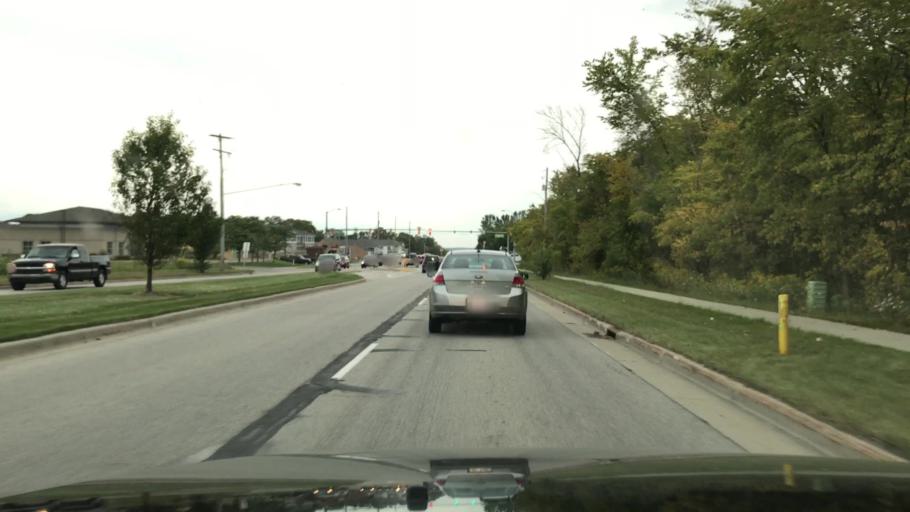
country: US
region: Michigan
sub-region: Kent County
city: Grandville
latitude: 42.8689
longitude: -85.7623
